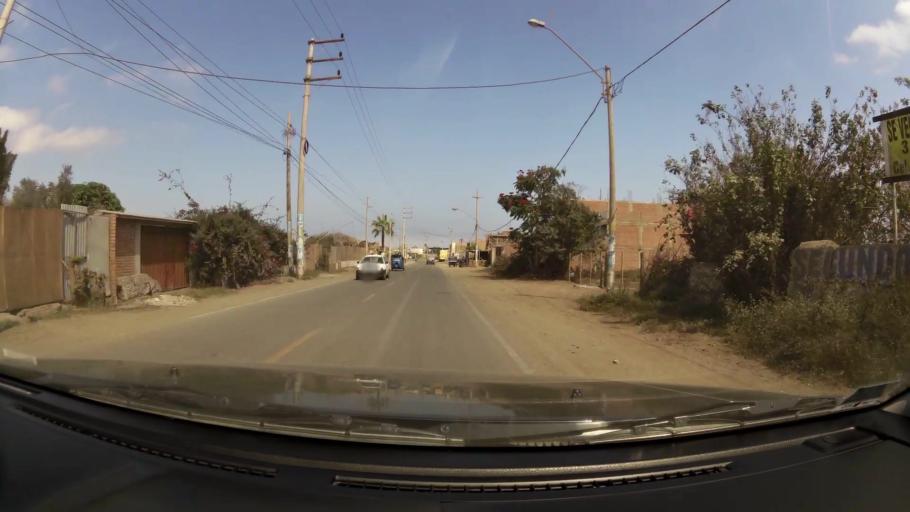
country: PE
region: Lima
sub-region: Provincia de Canete
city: Mala
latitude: -12.6636
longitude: -76.6397
